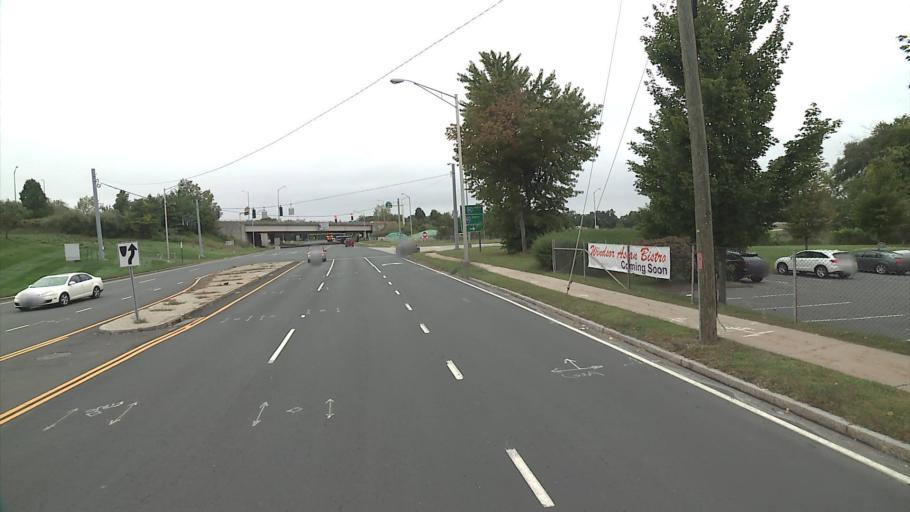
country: US
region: Connecticut
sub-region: Hartford County
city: Windsor
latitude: 41.8727
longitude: -72.6607
